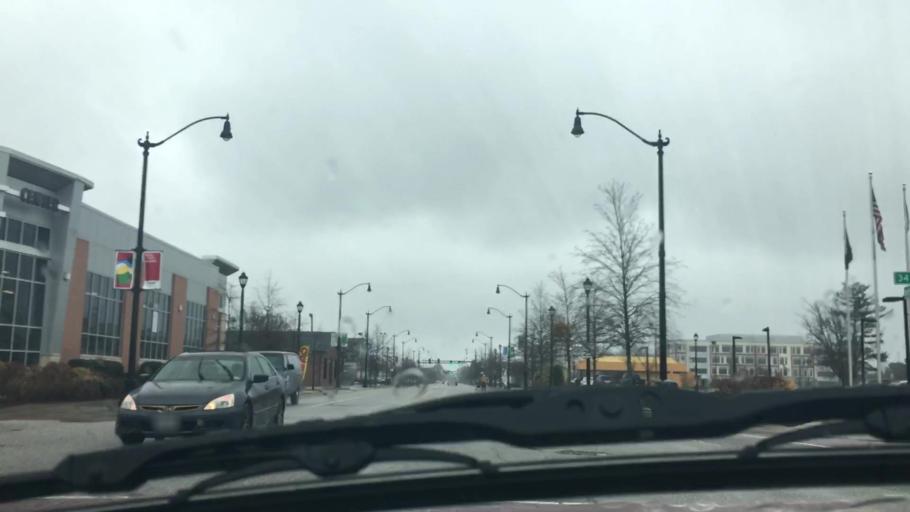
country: US
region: Virginia
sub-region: City of Newport News
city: Newport News
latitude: 36.9873
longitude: -76.4247
